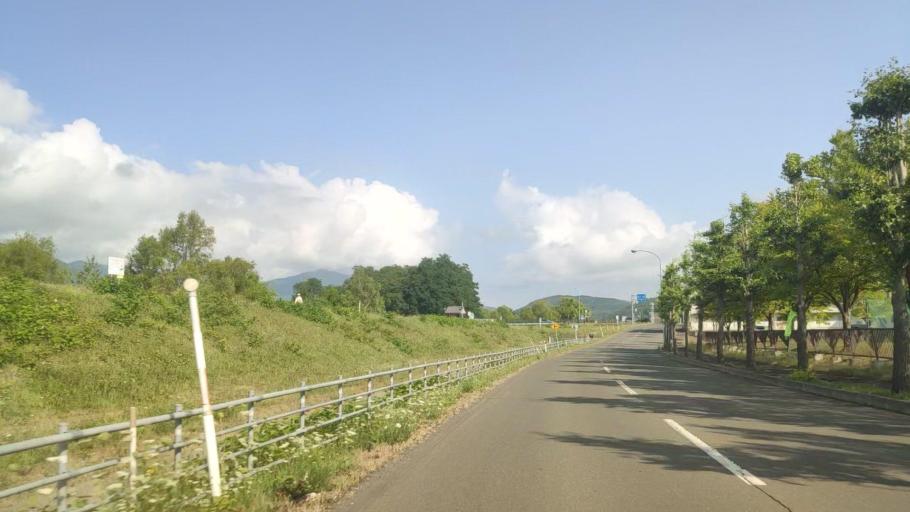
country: JP
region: Hokkaido
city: Shimo-furano
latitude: 43.3435
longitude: 142.3769
